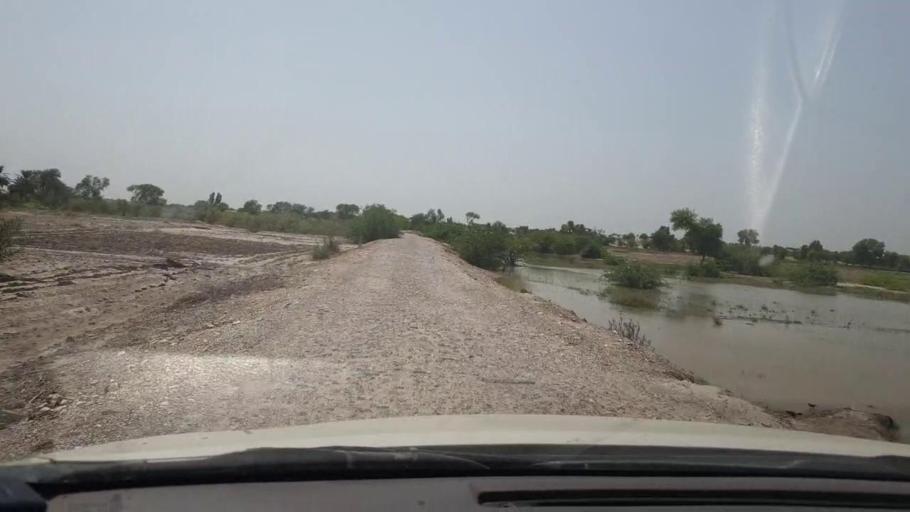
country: PK
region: Sindh
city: Rohri
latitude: 27.5212
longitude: 69.0954
